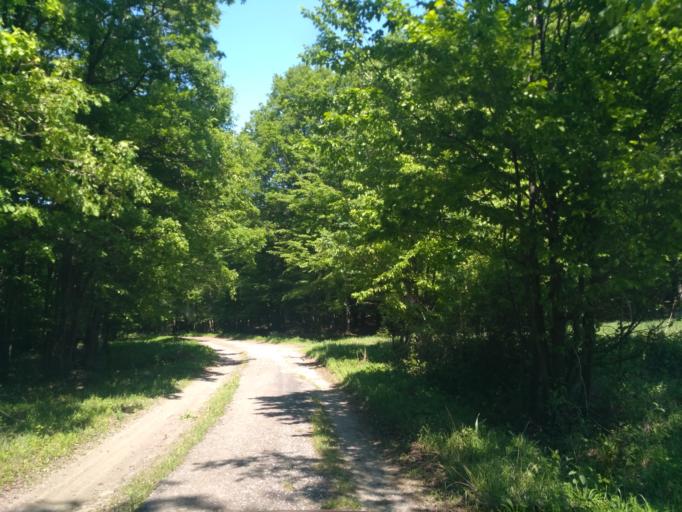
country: SK
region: Presovsky
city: Vranov nad Topl'ou
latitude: 48.8400
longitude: 21.4811
